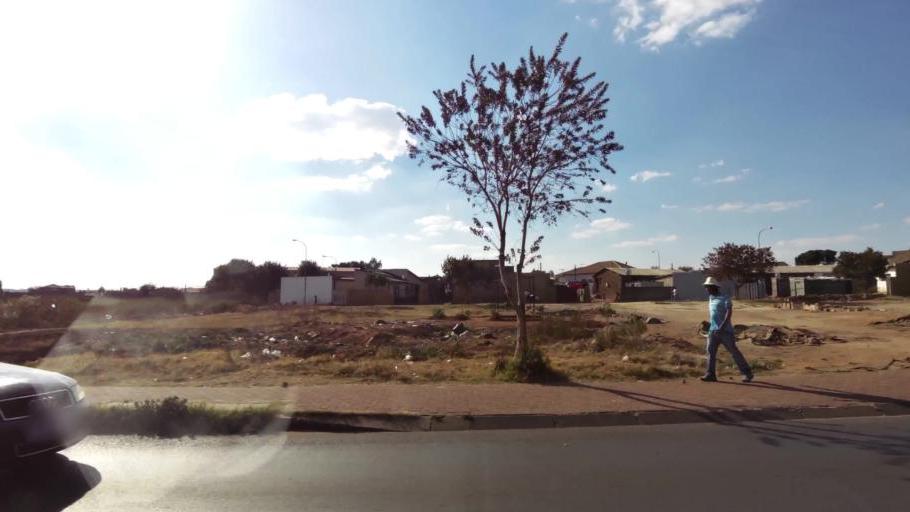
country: ZA
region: Gauteng
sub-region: City of Johannesburg Metropolitan Municipality
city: Soweto
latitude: -26.2247
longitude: 27.8839
